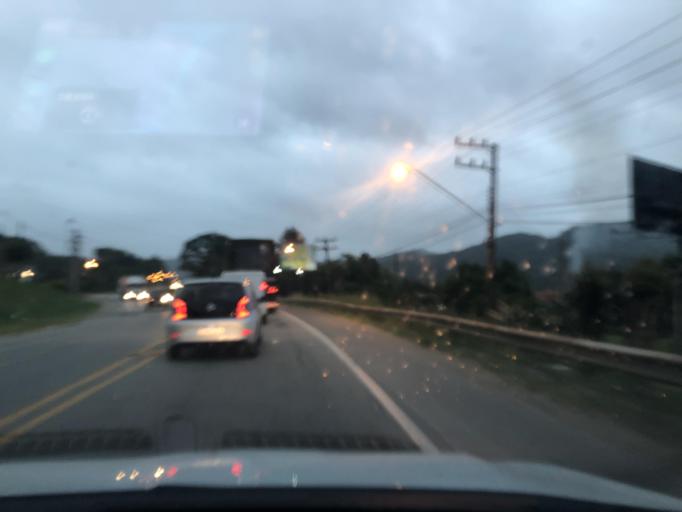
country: BR
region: Santa Catarina
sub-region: Pomerode
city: Pomerode
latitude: -26.7854
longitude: -49.0853
